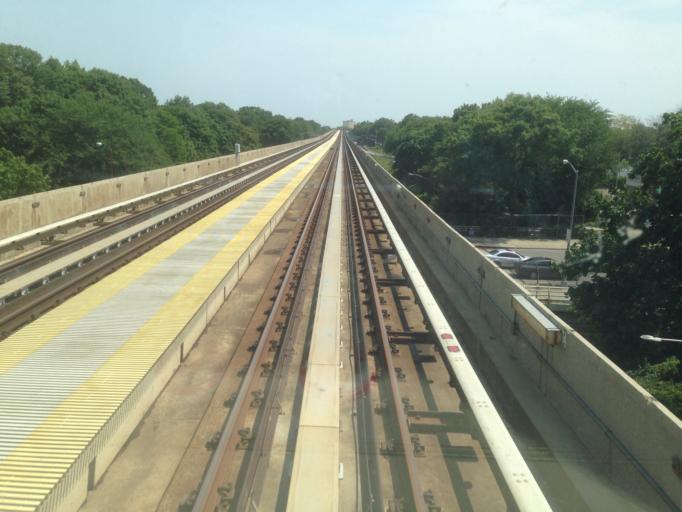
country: US
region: New York
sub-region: Queens County
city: Jamaica
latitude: 40.6833
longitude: -73.8058
